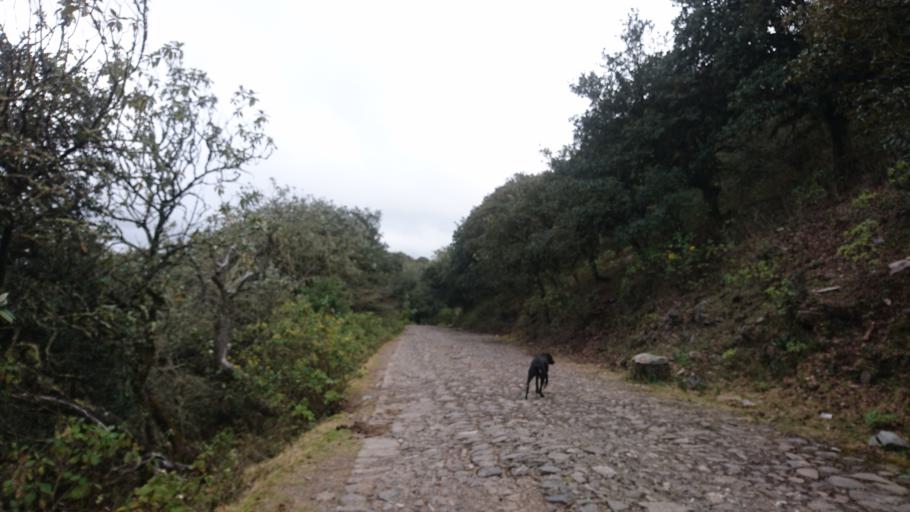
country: MX
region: San Luis Potosi
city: Zaragoza
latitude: 22.0742
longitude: -100.6392
